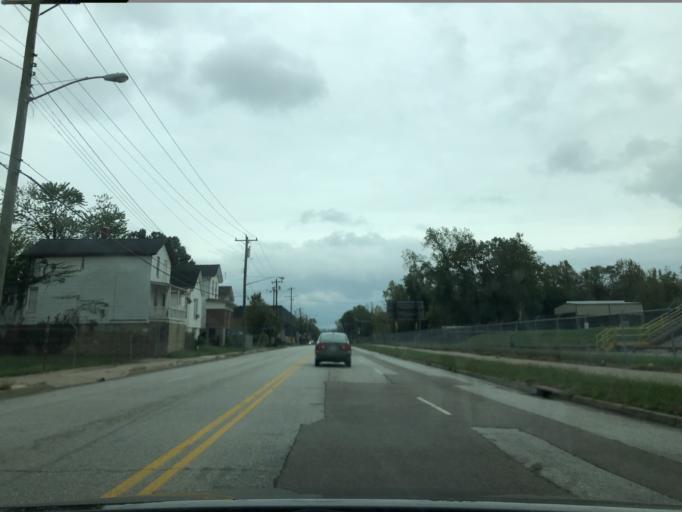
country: US
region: Kentucky
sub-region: Campbell County
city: Dayton
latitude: 39.1099
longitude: -84.4378
